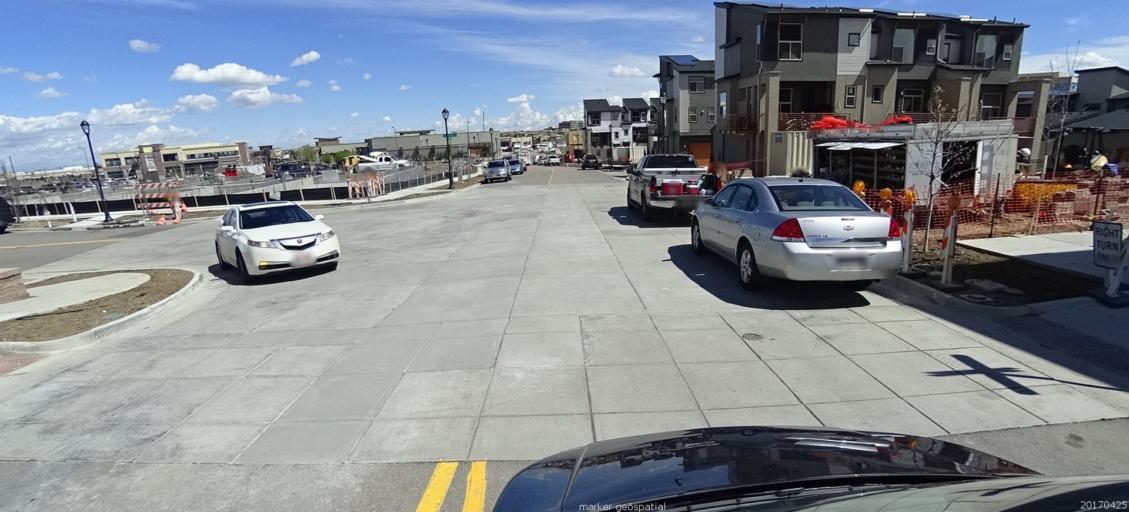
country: US
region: Colorado
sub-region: Adams County
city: Lone Tree
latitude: 39.5324
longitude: -104.8803
